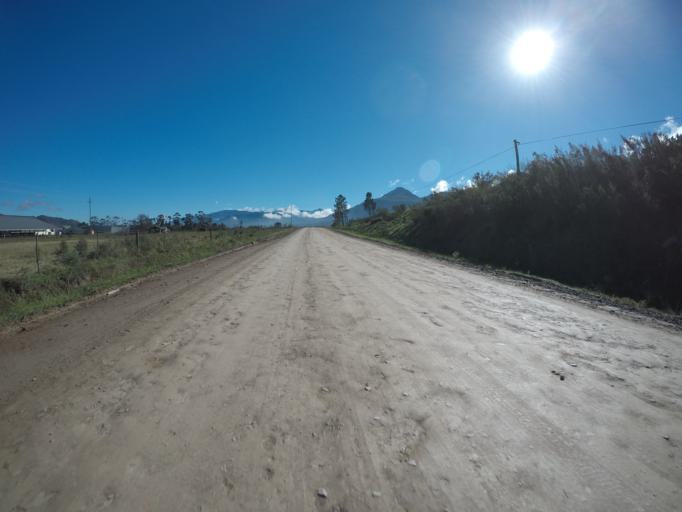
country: ZA
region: Western Cape
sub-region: Overberg District Municipality
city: Caledon
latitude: -34.0702
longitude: 19.6332
